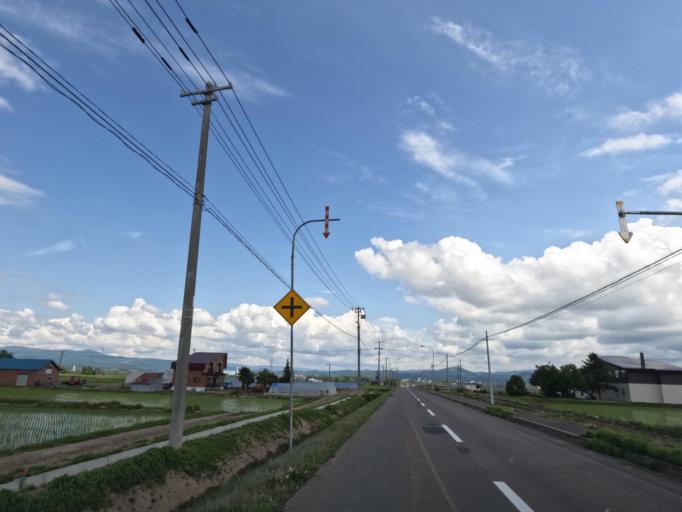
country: JP
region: Hokkaido
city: Takikawa
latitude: 43.5752
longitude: 141.8519
